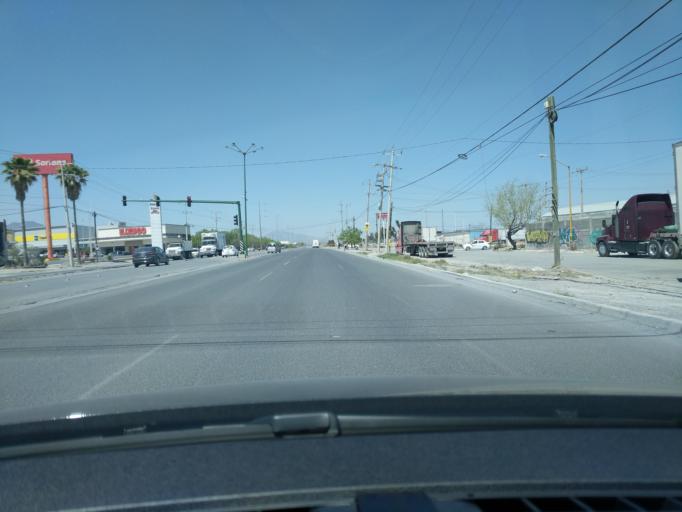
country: MX
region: Nuevo Leon
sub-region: Salinas Victoria
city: Emiliano Zapata
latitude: 25.8913
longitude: -100.2588
